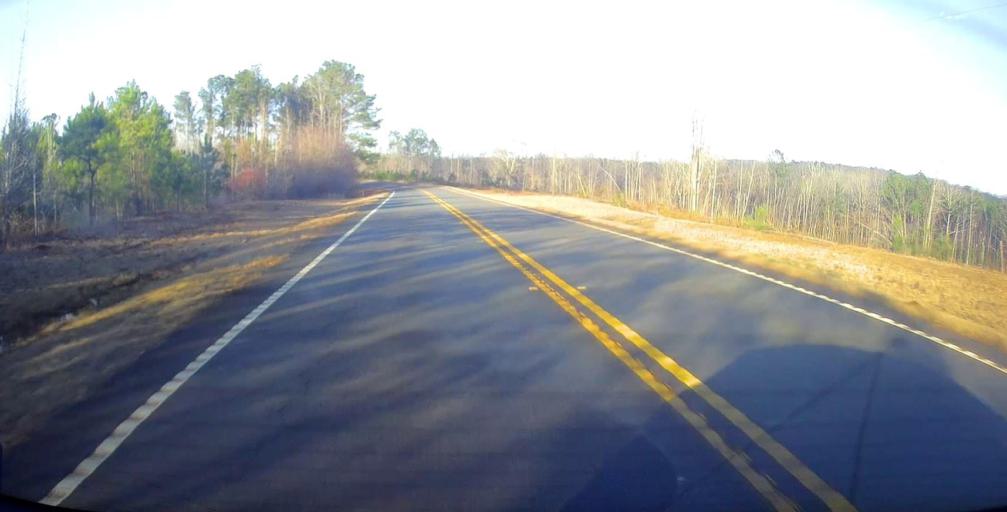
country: US
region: Georgia
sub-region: Upson County
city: Thomaston
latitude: 32.8450
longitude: -84.4176
